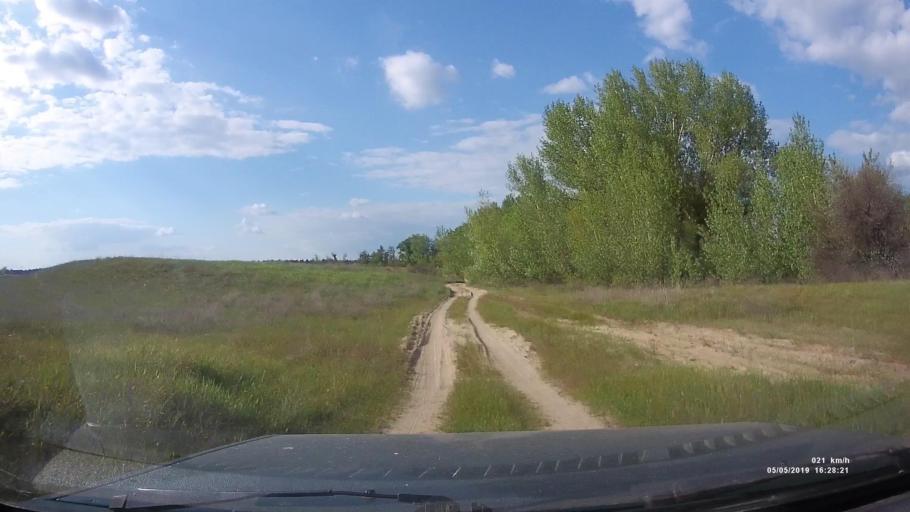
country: RU
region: Rostov
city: Ust'-Donetskiy
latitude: 47.7673
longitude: 41.0159
